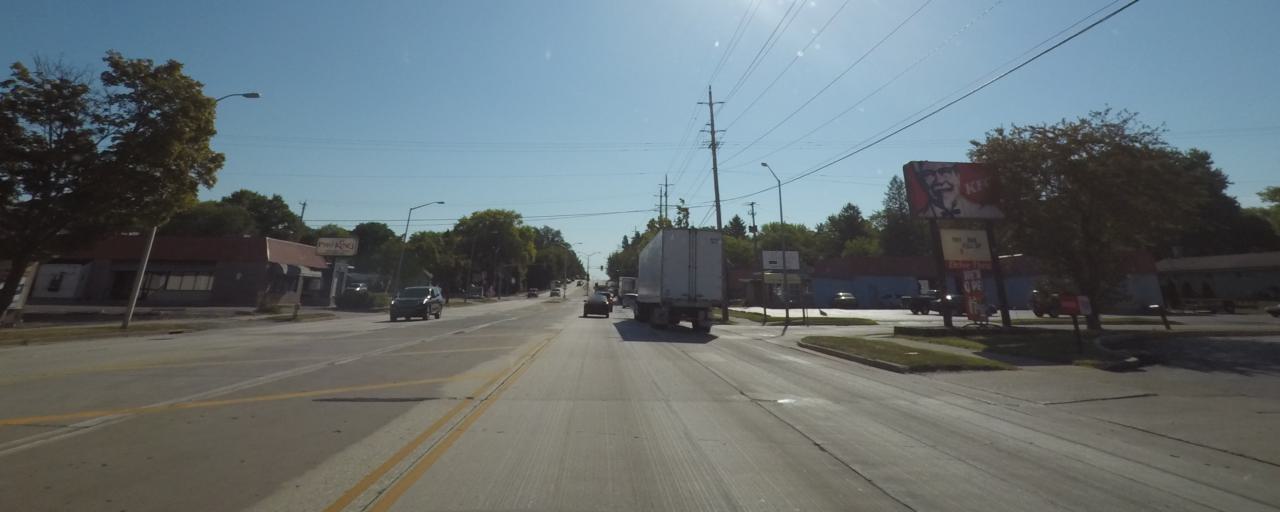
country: US
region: Wisconsin
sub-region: Waukesha County
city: Waukesha
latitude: 42.9883
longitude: -88.2340
